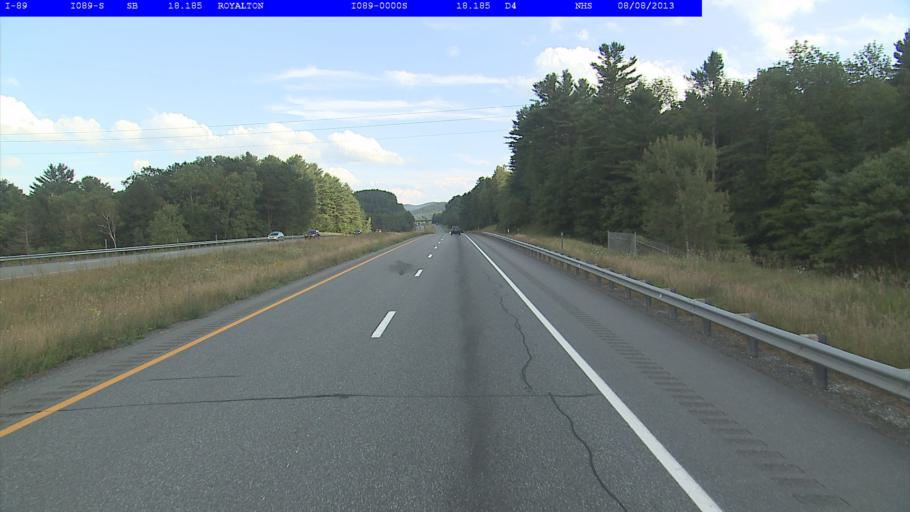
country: US
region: Vermont
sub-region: Orange County
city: Randolph
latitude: 43.8165
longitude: -72.5244
